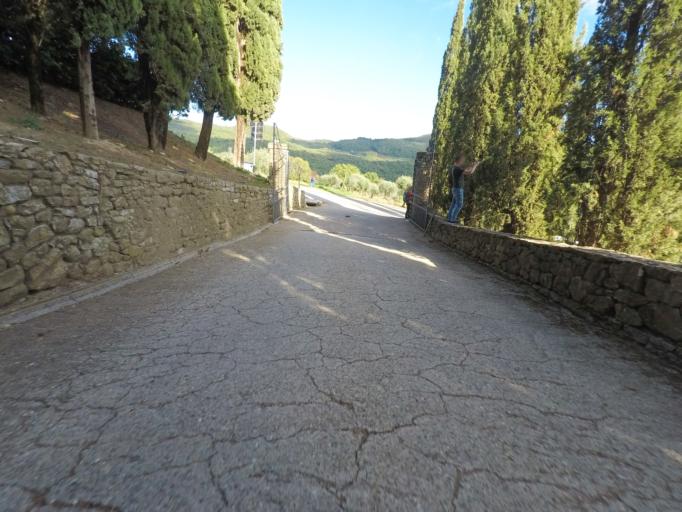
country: IT
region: Tuscany
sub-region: Provincia di Siena
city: Radda in Chianti
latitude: 43.5191
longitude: 11.4035
